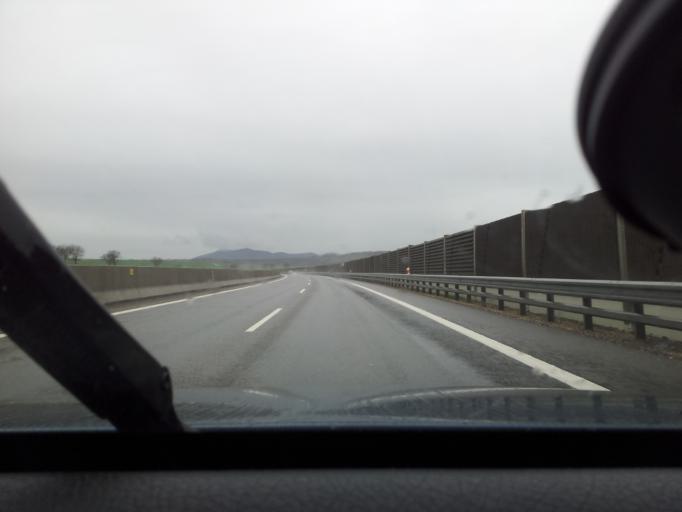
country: SK
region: Nitriansky
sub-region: Okres Nitra
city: Vrable
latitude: 48.3391
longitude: 18.2433
